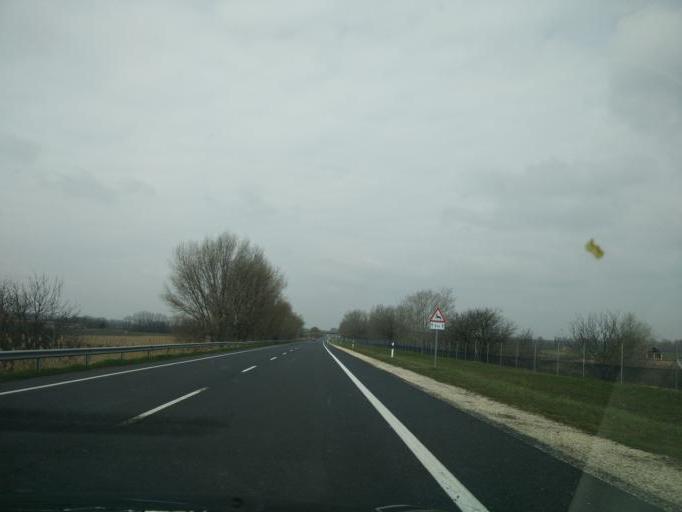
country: HU
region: Gyor-Moson-Sopron
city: Toltestava
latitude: 47.6973
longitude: 17.7773
